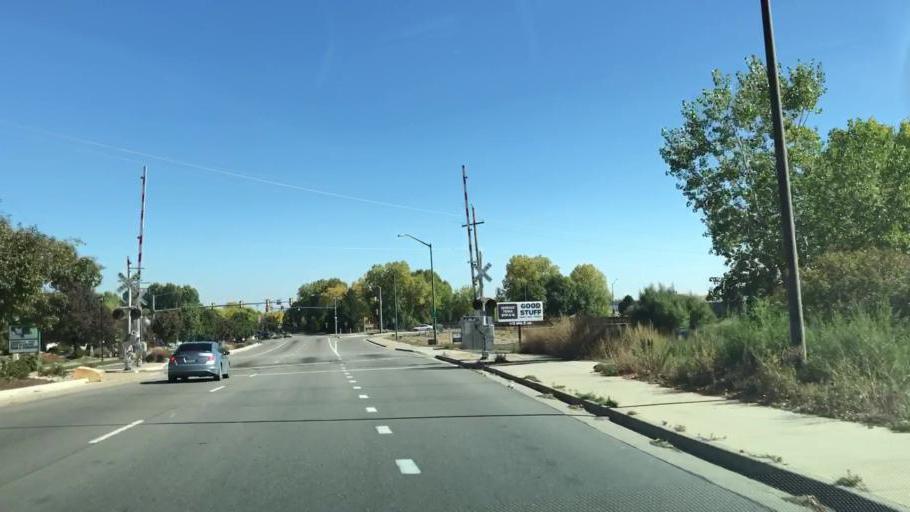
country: US
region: Colorado
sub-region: Larimer County
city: Fort Collins
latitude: 40.5707
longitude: -105.0398
